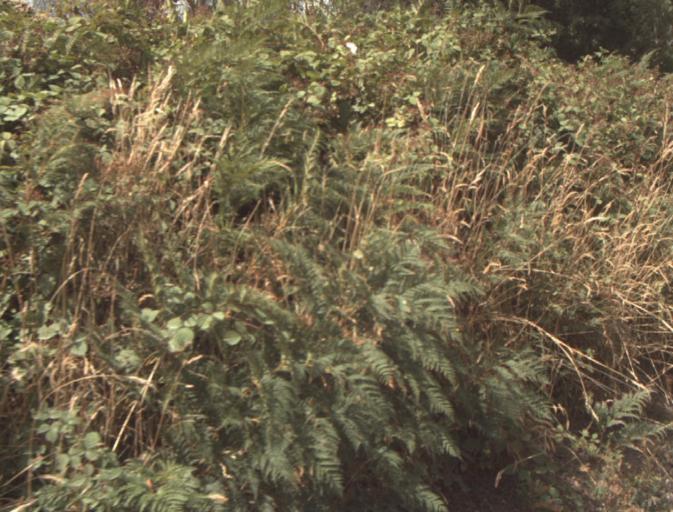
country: AU
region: Tasmania
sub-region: Launceston
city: Mayfield
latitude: -41.1948
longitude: 147.1702
